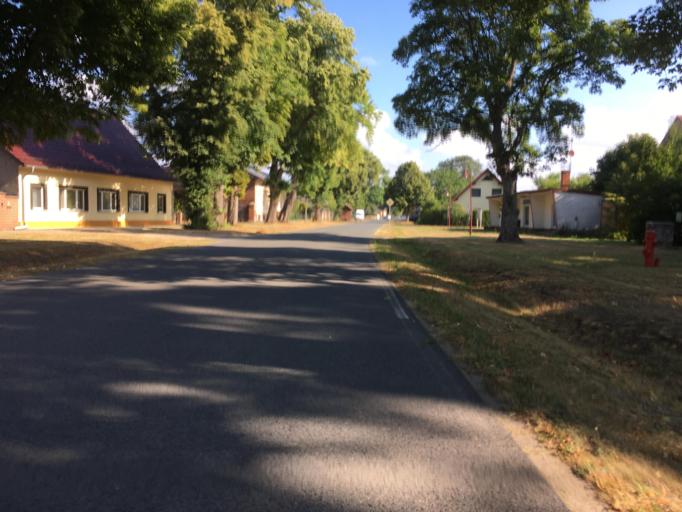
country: DE
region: Brandenburg
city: Liebenwalde
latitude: 52.9109
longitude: 13.4609
